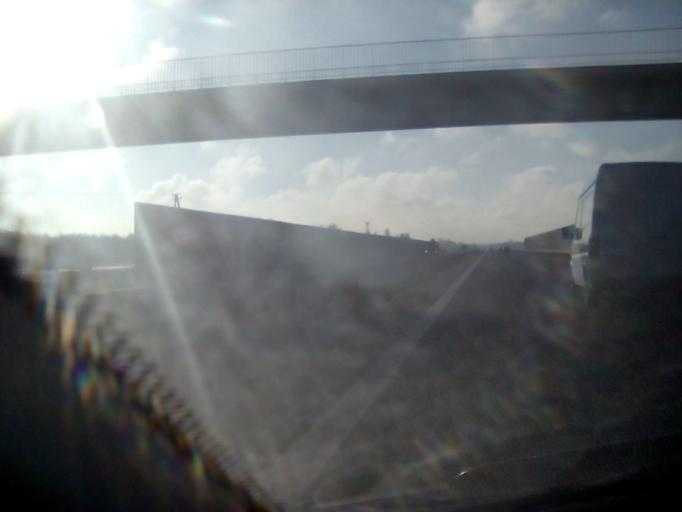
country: PL
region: Masovian Voivodeship
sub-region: Powiat grojecki
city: Grojec
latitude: 51.8141
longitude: 20.8843
